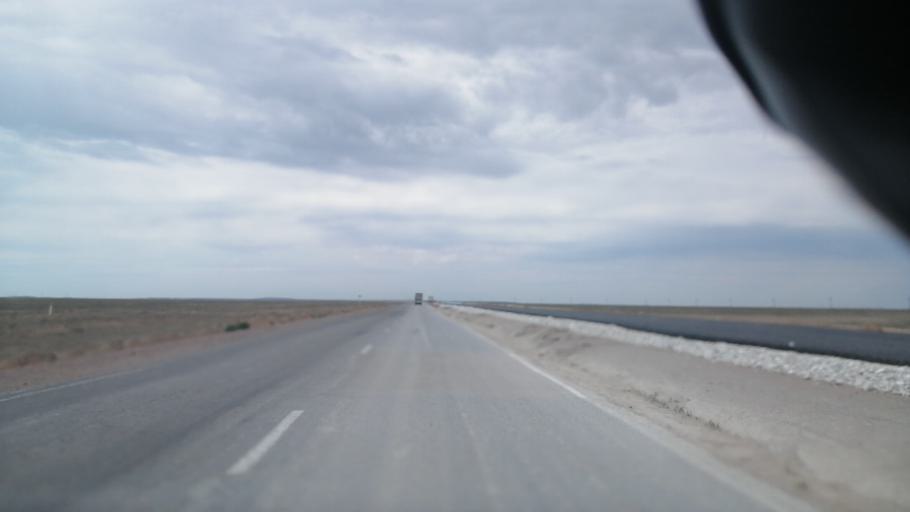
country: KZ
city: Priozersk
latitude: 46.5418
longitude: 74.1640
